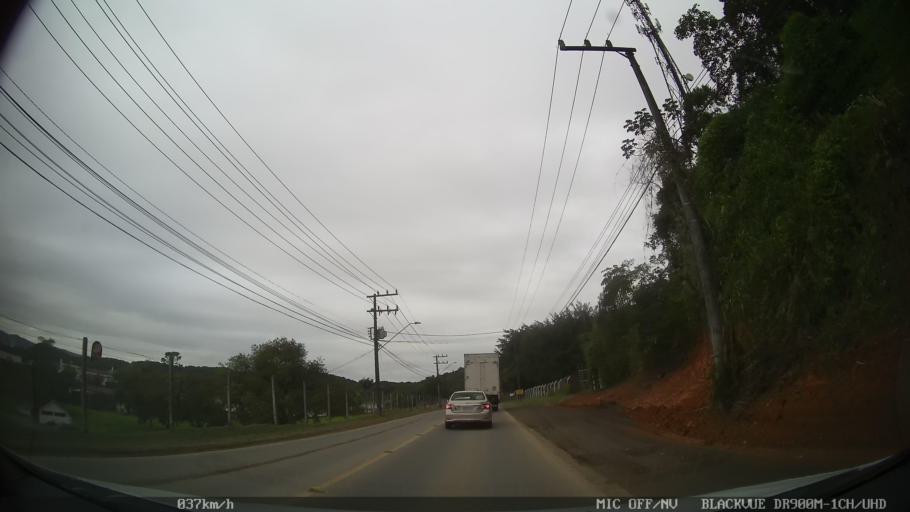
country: BR
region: Santa Catarina
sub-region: Joinville
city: Joinville
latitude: -26.2428
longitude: -48.8877
